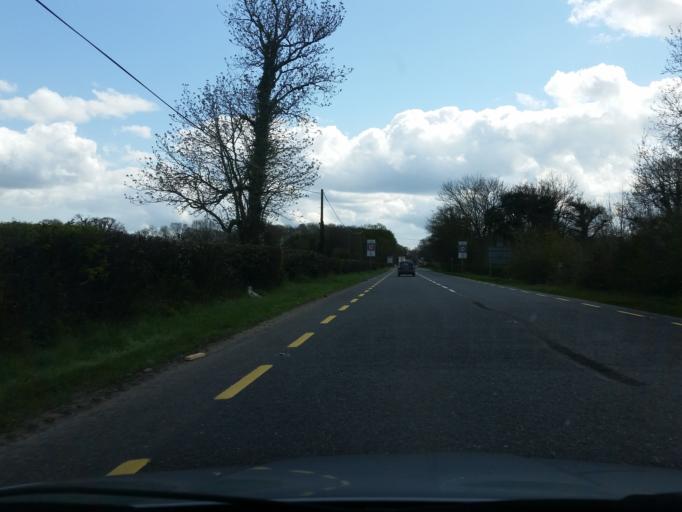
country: IE
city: Kentstown
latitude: 53.6442
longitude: -6.5048
